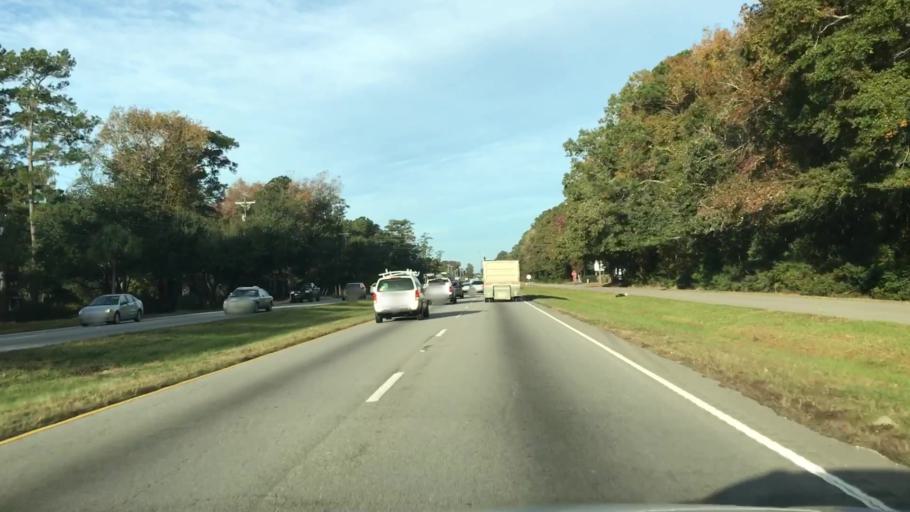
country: US
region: South Carolina
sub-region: Charleston County
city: Shell Point
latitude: 32.7978
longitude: -80.0862
